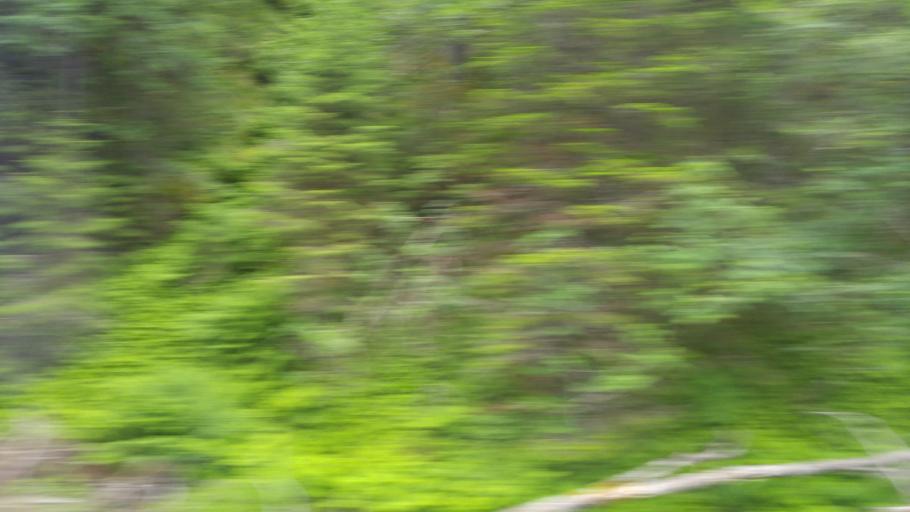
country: NO
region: Nord-Trondelag
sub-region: Meraker
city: Meraker
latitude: 63.4616
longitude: 11.5277
